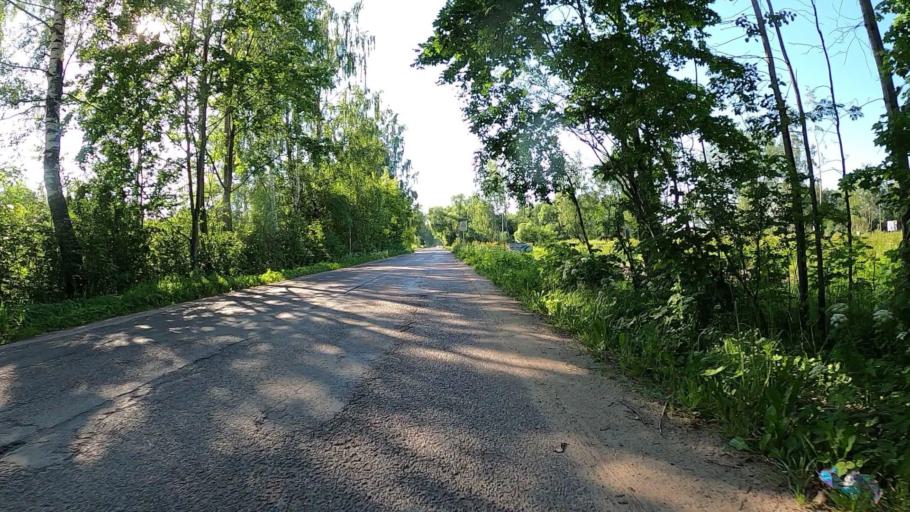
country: LV
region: Kekava
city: Kekava
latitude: 56.8831
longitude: 24.2575
